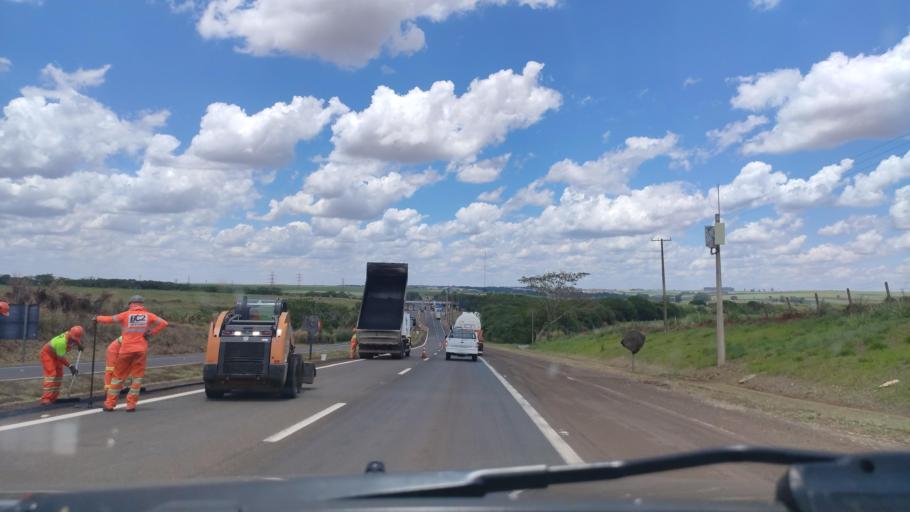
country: BR
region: Sao Paulo
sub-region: Pederneiras
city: Pederneiras
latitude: -22.3148
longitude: -48.7209
